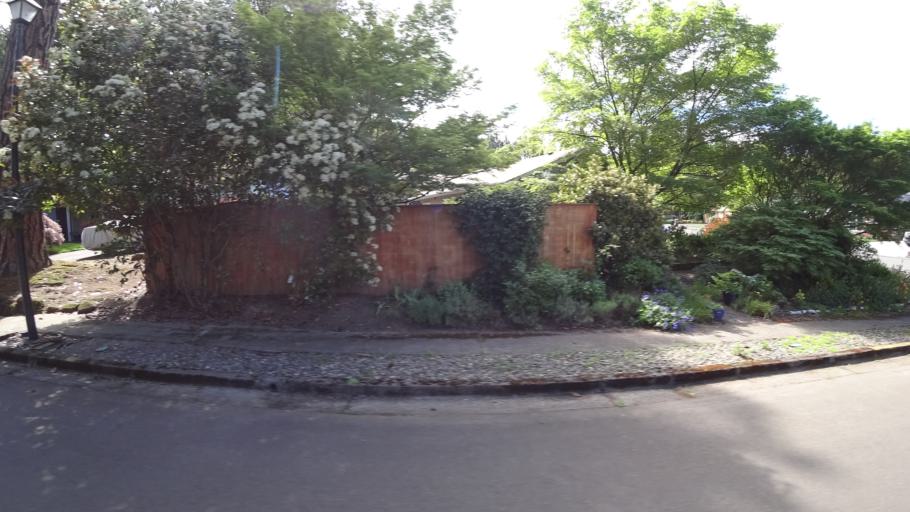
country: US
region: Oregon
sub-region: Washington County
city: Beaverton
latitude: 45.4659
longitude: -122.8171
